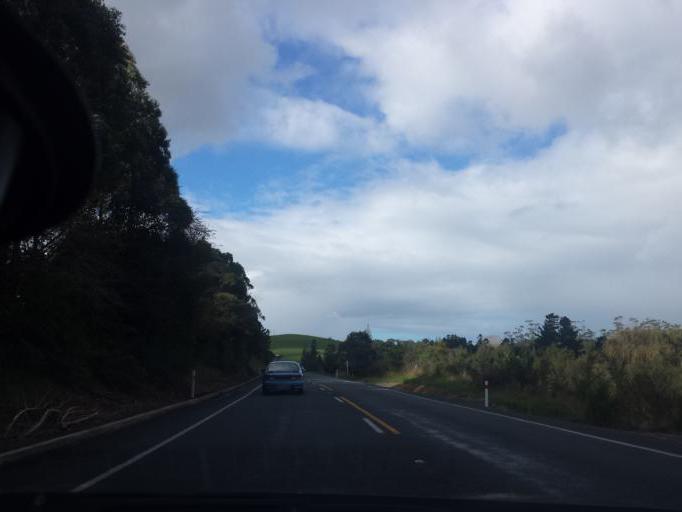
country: NZ
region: Auckland
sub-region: Auckland
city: Warkworth
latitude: -36.4000
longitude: 174.6972
